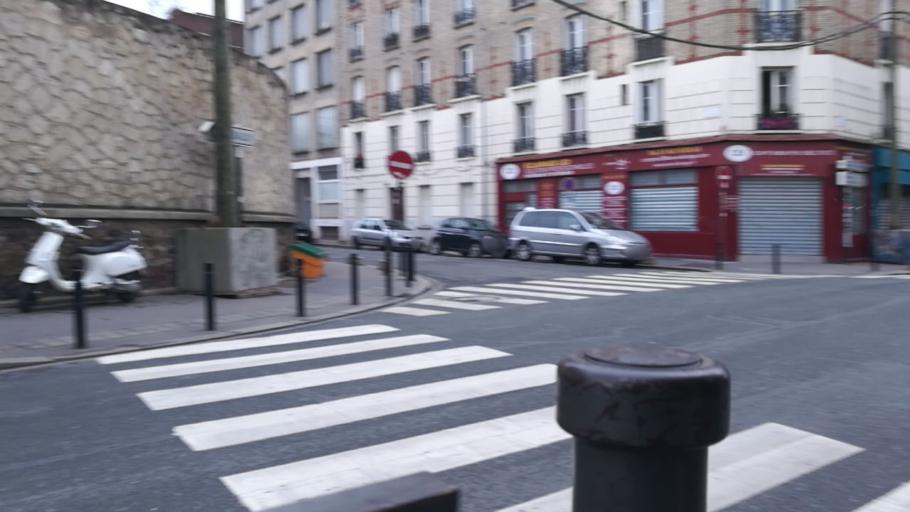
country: FR
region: Ile-de-France
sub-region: Paris
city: Saint-Ouen
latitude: 48.9055
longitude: 2.3370
